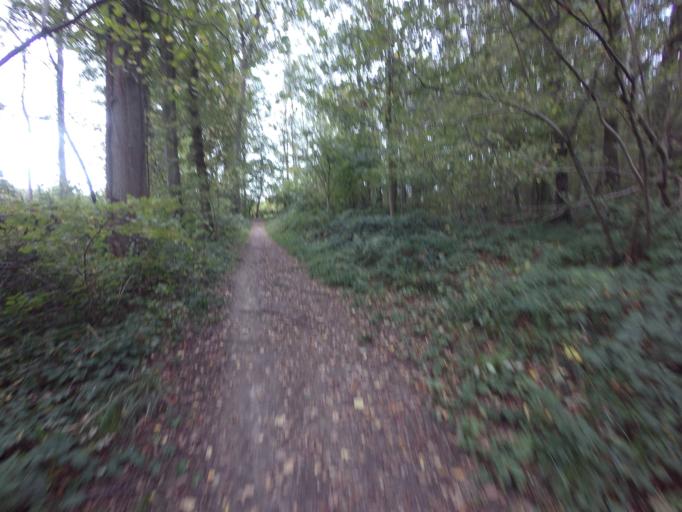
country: NL
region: Limburg
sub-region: Valkenburg aan de Geul
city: Schin op Geul
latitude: 50.7943
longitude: 5.8949
